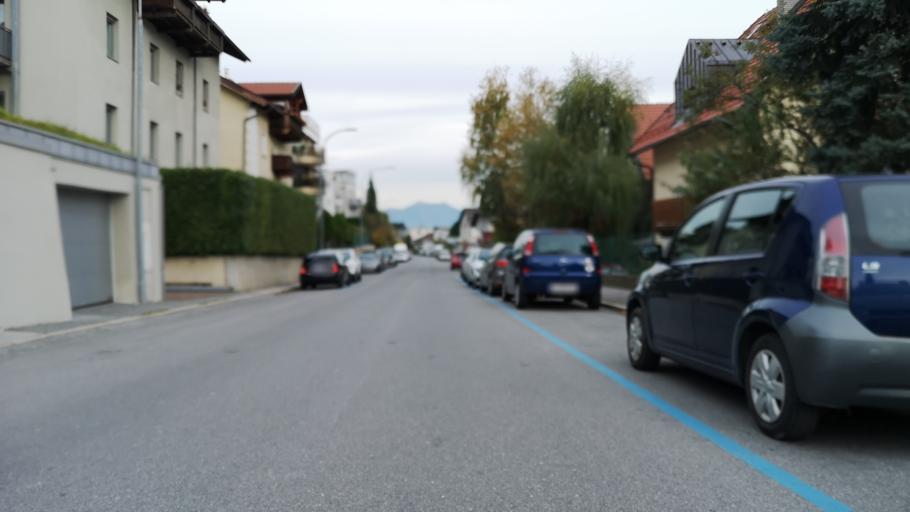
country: AT
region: Tyrol
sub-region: Innsbruck Stadt
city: Innsbruck
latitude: 47.2686
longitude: 11.3749
